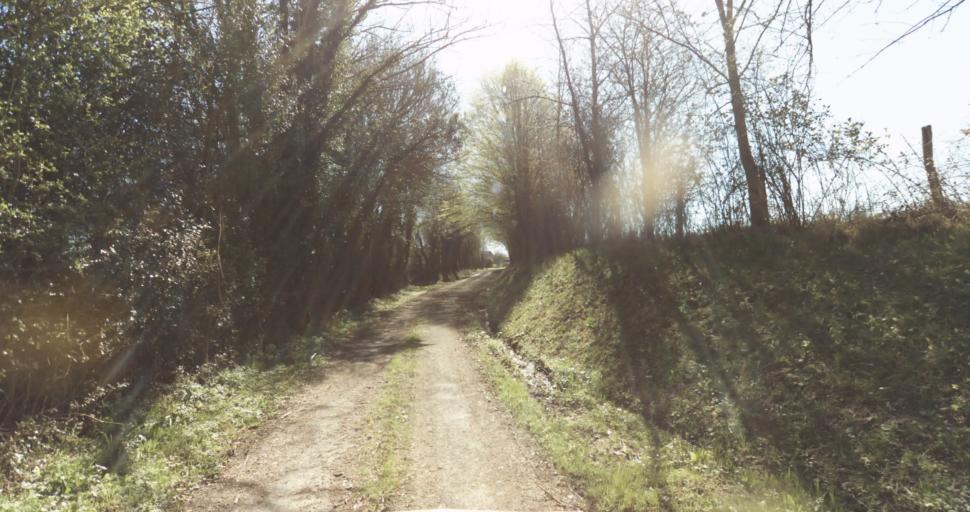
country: FR
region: Lower Normandy
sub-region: Departement du Calvados
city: Livarot
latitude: 49.0150
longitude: 0.0925
